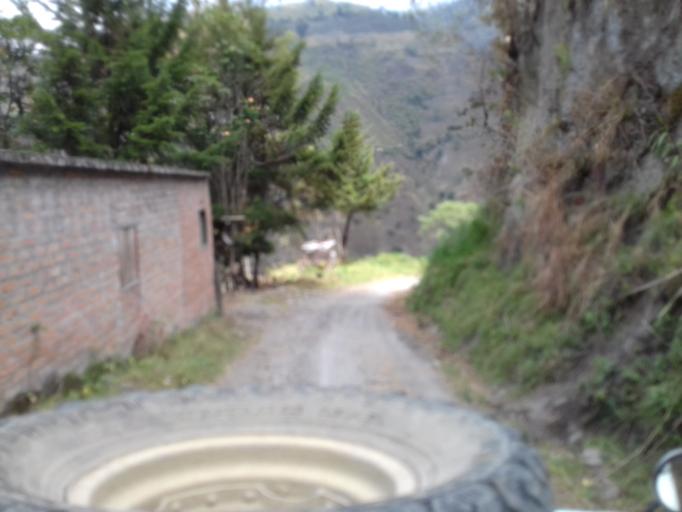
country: CO
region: Tolima
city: Cajamarca
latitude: 4.5019
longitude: -75.3952
